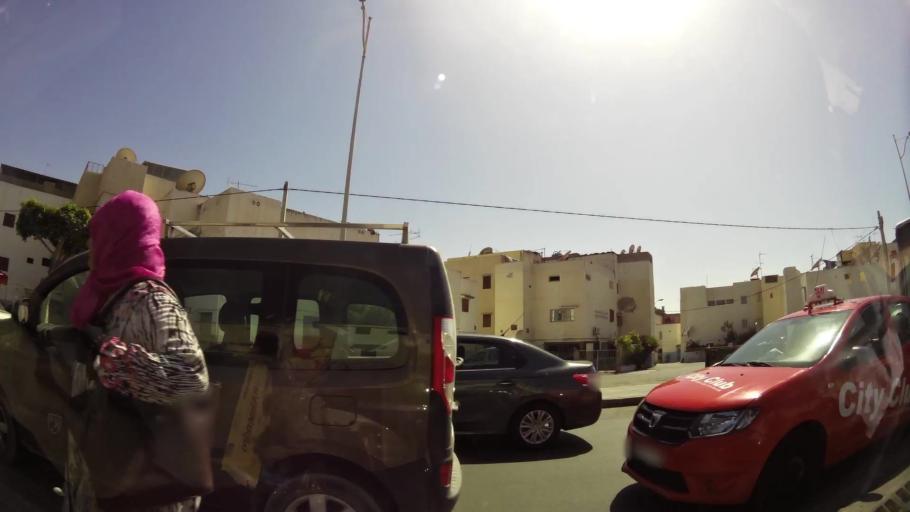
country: MA
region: Oued ed Dahab-Lagouira
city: Dakhla
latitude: 30.4155
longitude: -9.5710
